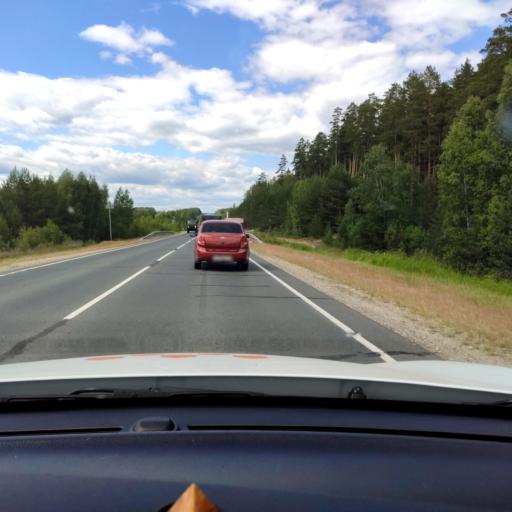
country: RU
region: Mariy-El
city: Volzhsk
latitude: 55.8955
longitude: 48.3940
